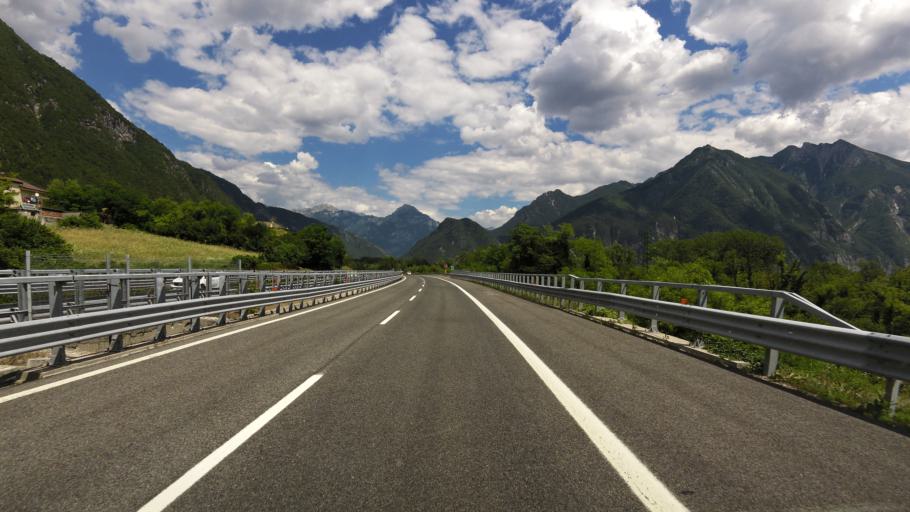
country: IT
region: Friuli Venezia Giulia
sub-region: Provincia di Udine
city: Amaro
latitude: 46.3716
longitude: 13.0997
